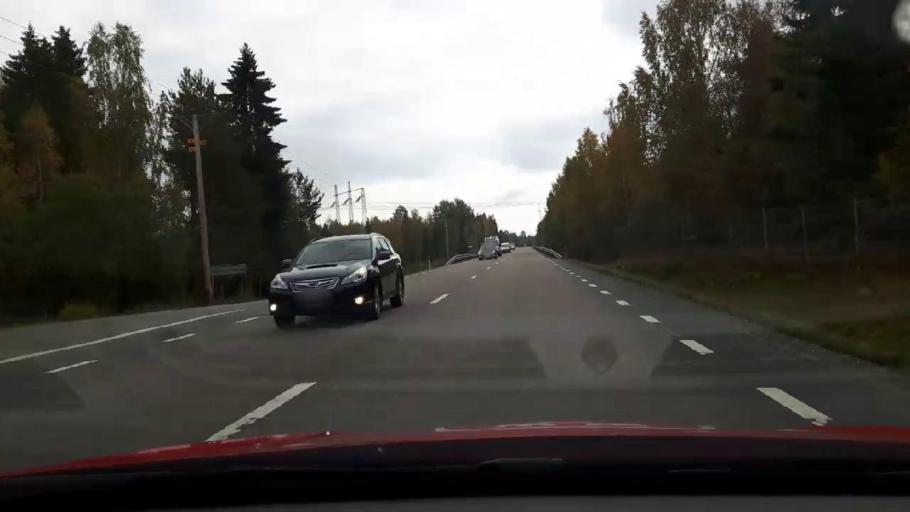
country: SE
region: Gaevleborg
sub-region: Bollnas Kommun
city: Kilafors
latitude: 61.2921
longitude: 16.5003
